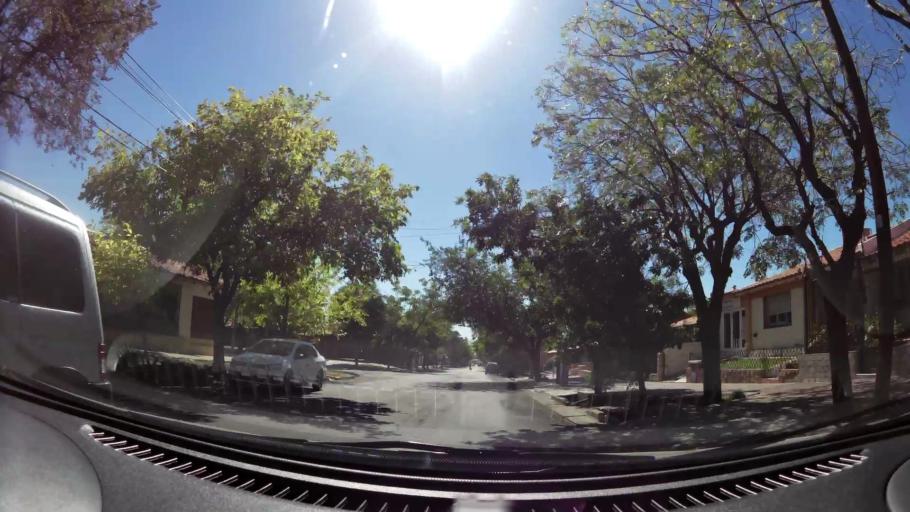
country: AR
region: Mendoza
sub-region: Departamento de Godoy Cruz
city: Godoy Cruz
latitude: -32.9166
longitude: -68.8728
